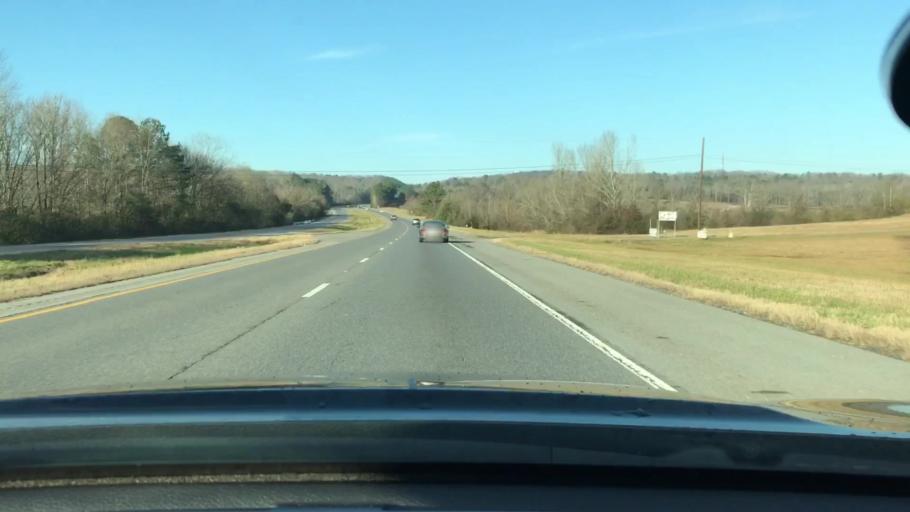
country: US
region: Alabama
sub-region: Shelby County
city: Harpersville
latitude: 33.3494
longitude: -86.4623
